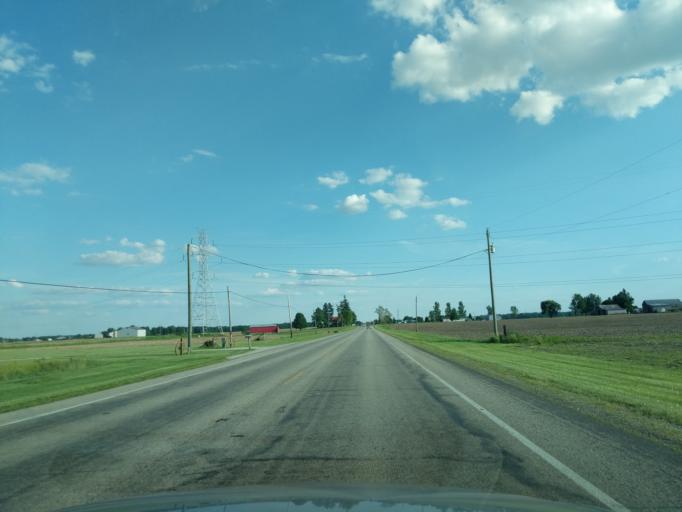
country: US
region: Indiana
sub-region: Whitley County
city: Columbia City
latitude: 41.0671
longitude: -85.4704
